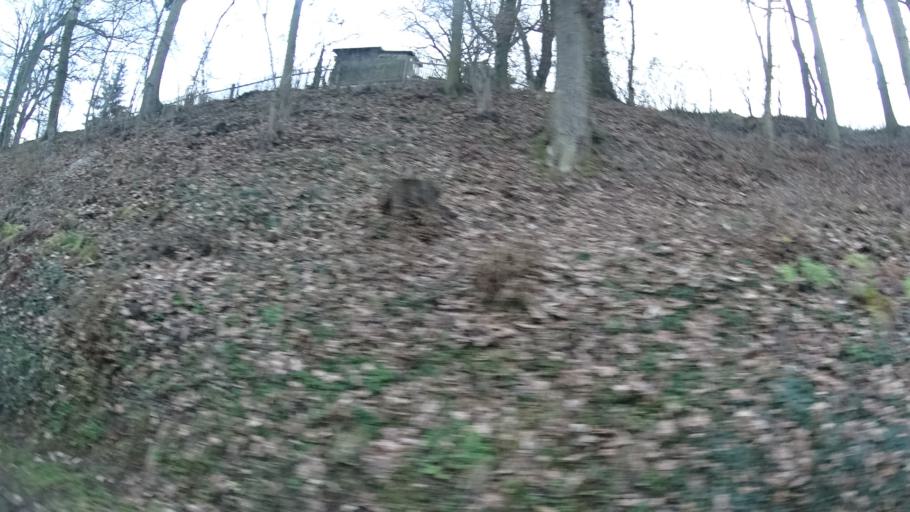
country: DE
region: Thuringia
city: Kahla
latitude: 50.8092
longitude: 11.5737
